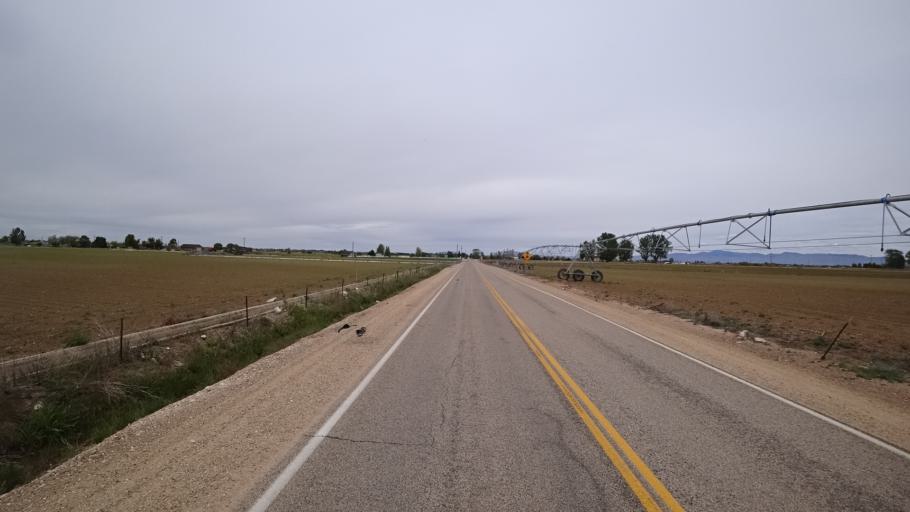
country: US
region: Idaho
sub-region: Ada County
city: Kuna
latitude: 43.5006
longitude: -116.3742
